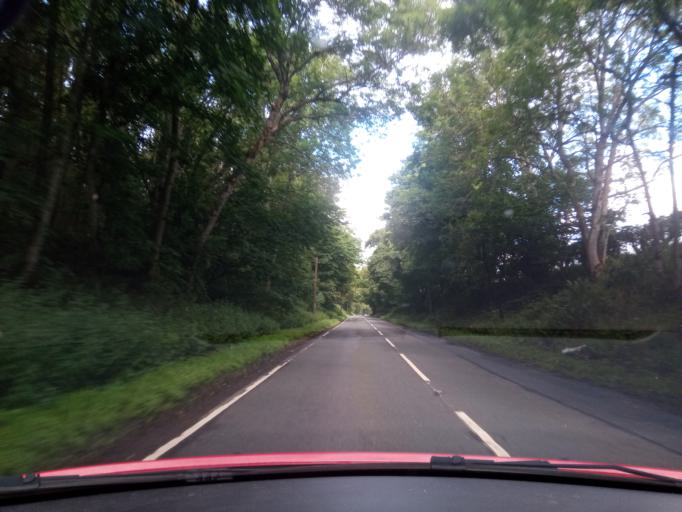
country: GB
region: Scotland
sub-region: The Scottish Borders
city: Lauder
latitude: 55.7217
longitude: -2.7241
